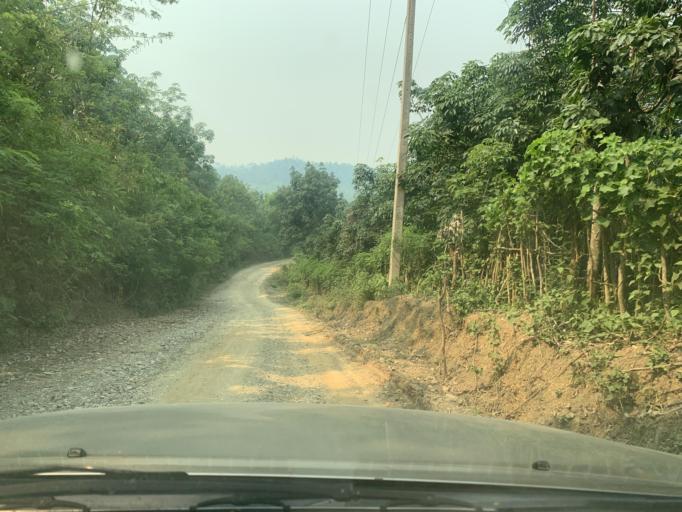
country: LA
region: Louangphabang
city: Louangphabang
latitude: 19.8970
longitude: 102.2546
